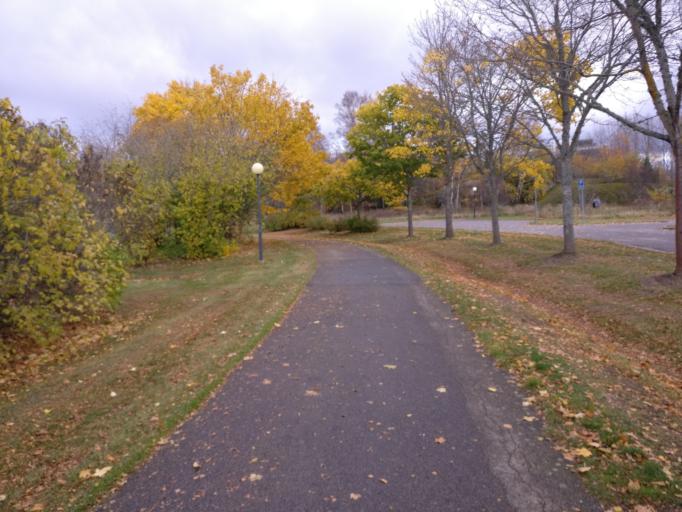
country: SE
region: OEstergoetland
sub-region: Linkopings Kommun
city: Malmslatt
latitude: 58.3918
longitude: 15.5614
